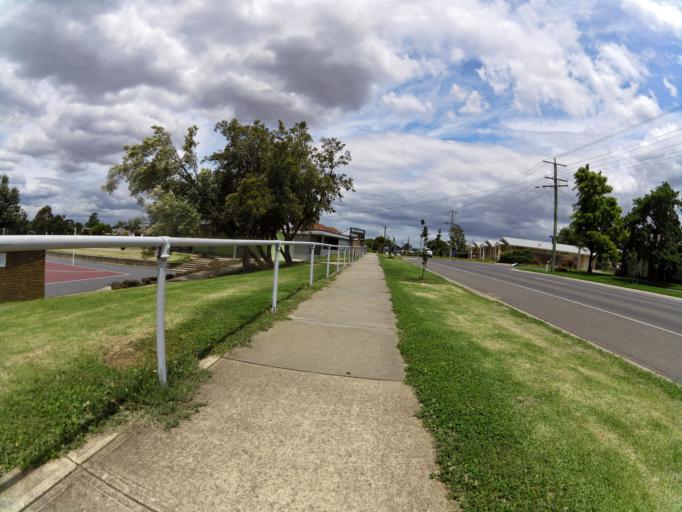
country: AU
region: Victoria
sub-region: Latrobe
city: Traralgon
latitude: -38.1885
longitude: 146.5344
